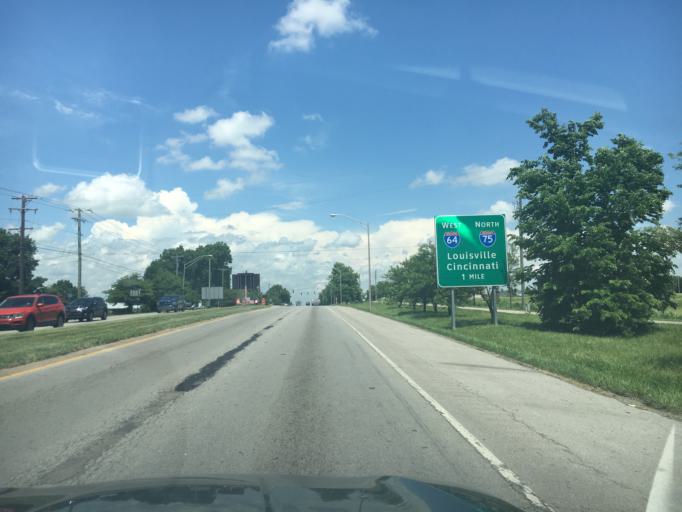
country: US
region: Kentucky
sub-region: Fayette County
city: Lexington-Fayette
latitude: 38.0832
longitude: -84.4914
